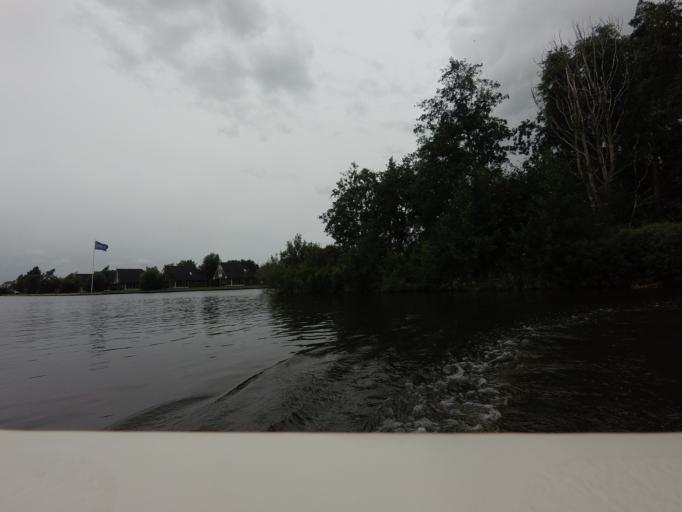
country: NL
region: Friesland
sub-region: Gemeente Boarnsterhim
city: Warten
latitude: 53.1230
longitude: 5.9420
